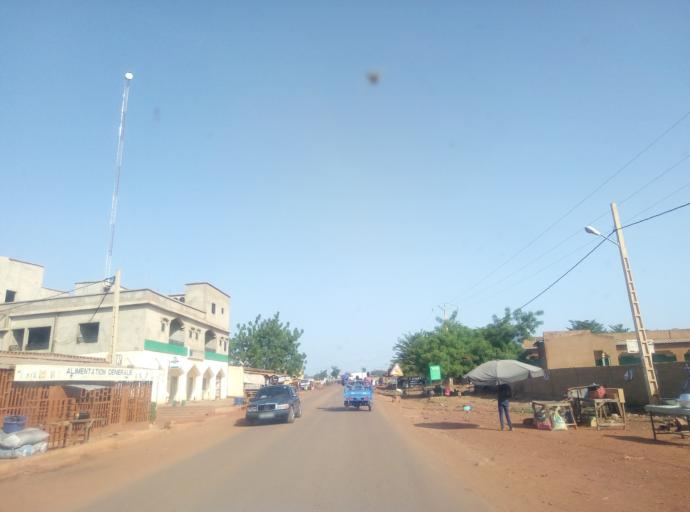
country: ML
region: Bamako
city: Bamako
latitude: 12.6111
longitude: -7.7751
